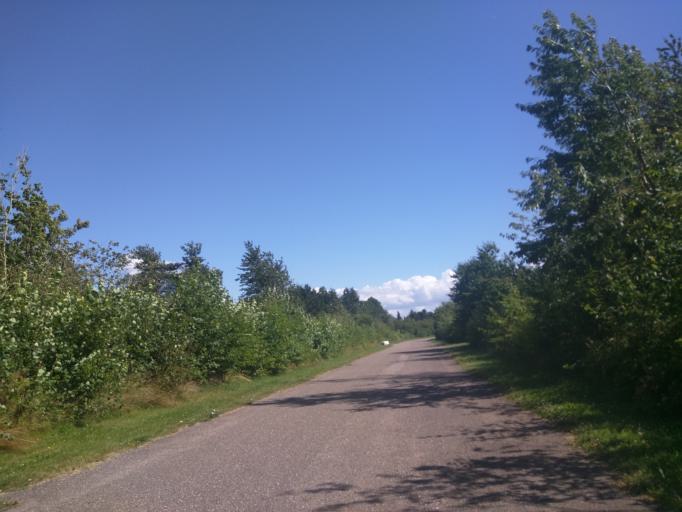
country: DK
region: Zealand
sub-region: Kalundborg Kommune
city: Svebolle
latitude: 55.6953
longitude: 11.2670
